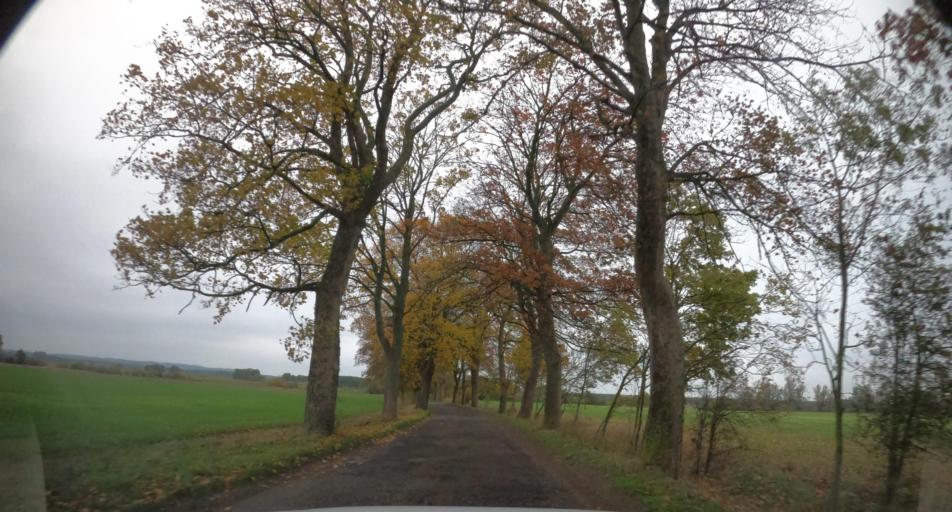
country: PL
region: West Pomeranian Voivodeship
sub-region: Powiat kamienski
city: Wolin
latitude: 53.9226
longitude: 14.6107
